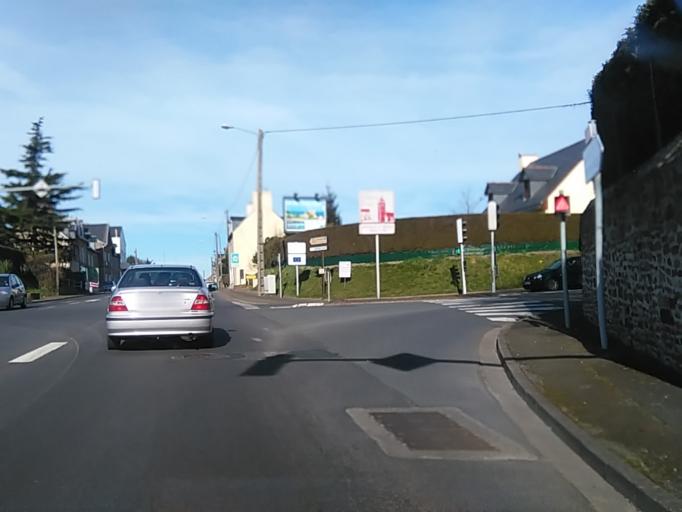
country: FR
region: Lower Normandy
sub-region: Departement de la Manche
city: Saint-Pair-sur-Mer
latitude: 48.8296
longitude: -1.5667
